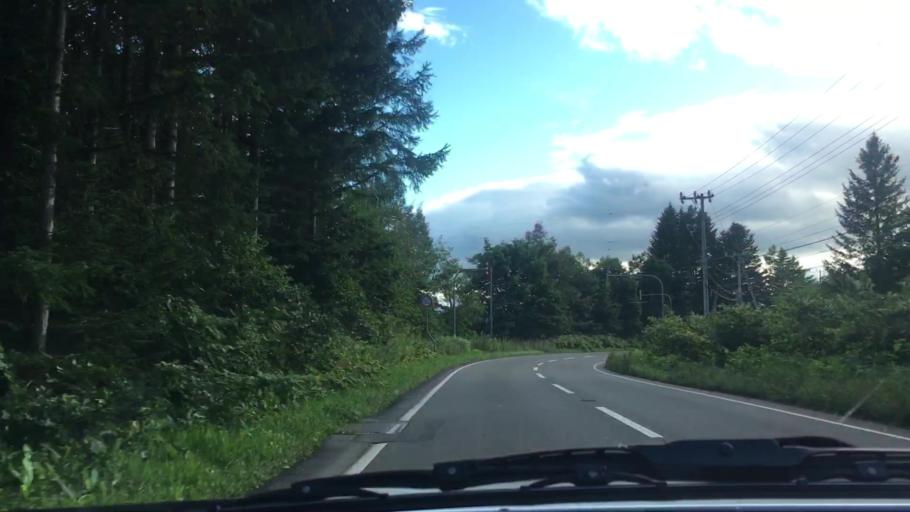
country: JP
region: Hokkaido
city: Otofuke
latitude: 43.1744
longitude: 142.9189
